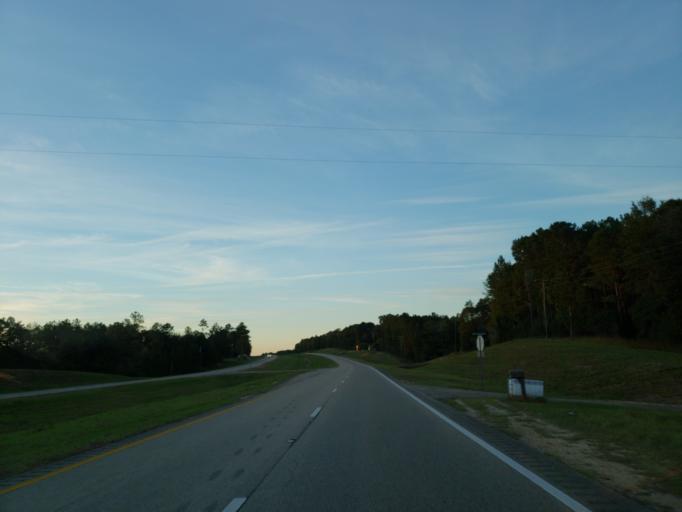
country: US
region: Mississippi
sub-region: Wayne County
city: Belmont
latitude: 31.4959
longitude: -88.4933
